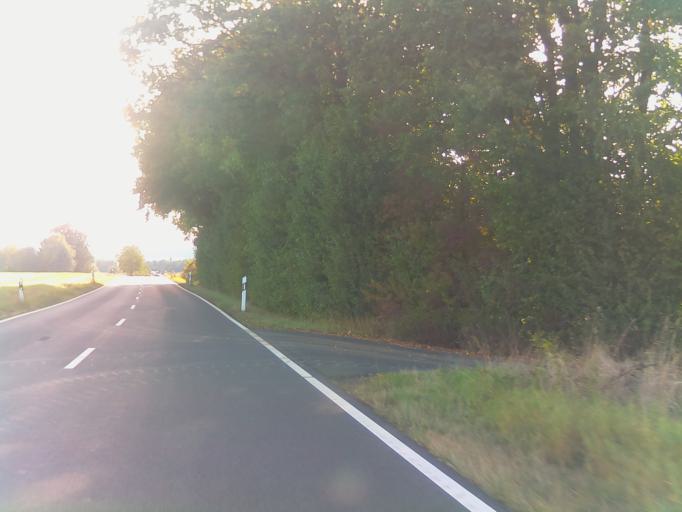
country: DE
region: Hesse
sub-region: Regierungsbezirk Giessen
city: Freiensteinau
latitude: 50.3557
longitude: 9.4048
